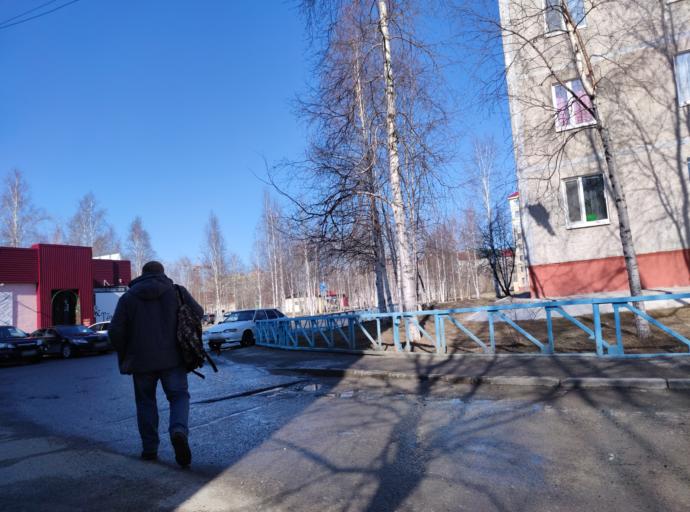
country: RU
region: Khanty-Mansiyskiy Avtonomnyy Okrug
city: Langepas
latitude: 61.2508
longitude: 75.1757
